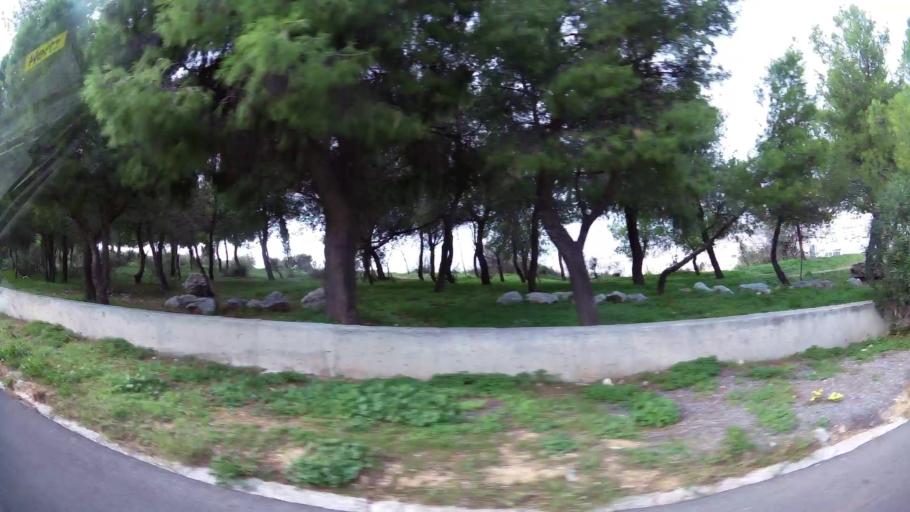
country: GR
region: Attica
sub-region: Nomarchia Athinas
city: Filothei
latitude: 38.0320
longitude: 23.7717
